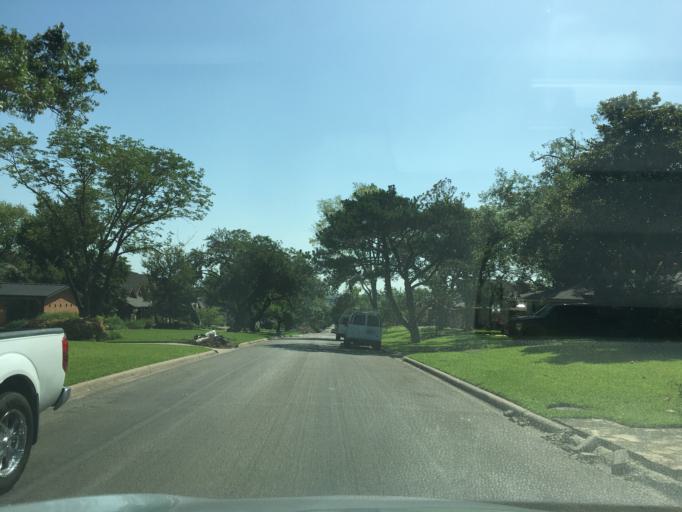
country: US
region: Texas
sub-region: Dallas County
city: University Park
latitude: 32.9041
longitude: -96.7783
